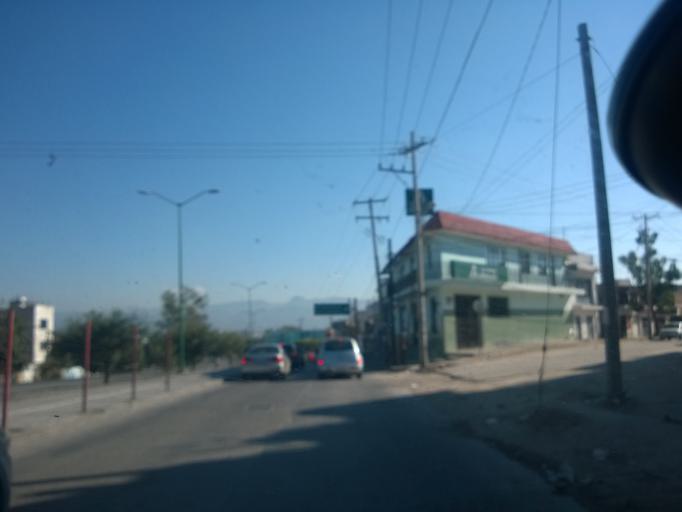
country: MX
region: Guanajuato
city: Leon
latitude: 21.1316
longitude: -101.7012
